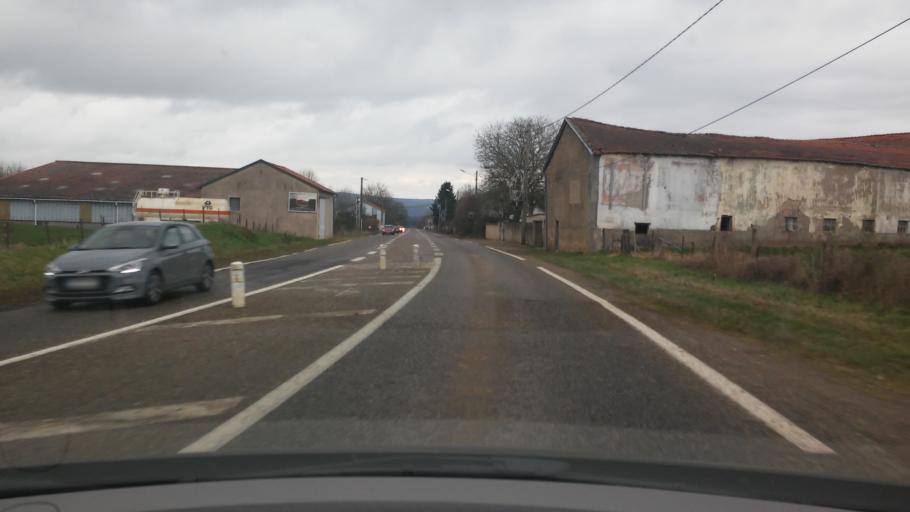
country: FR
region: Lorraine
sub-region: Departement de la Moselle
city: Retonfey
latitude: 49.1139
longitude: 6.3521
